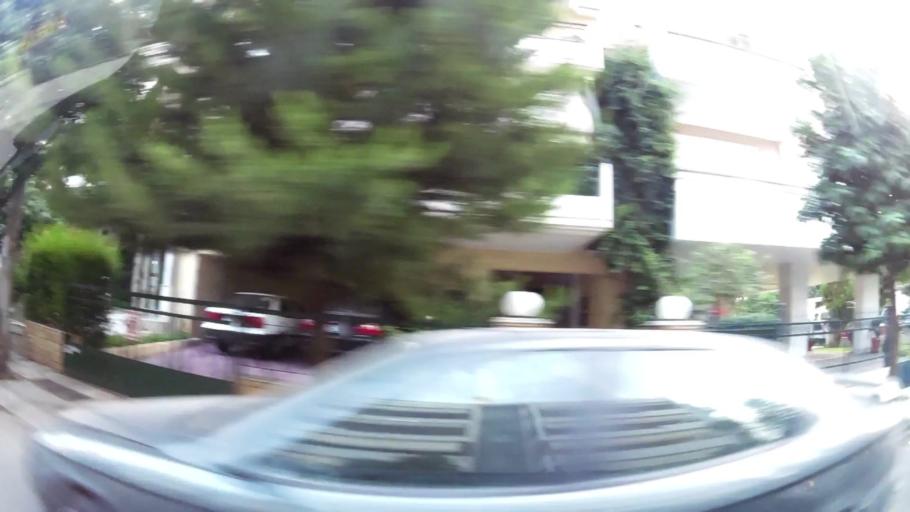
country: GR
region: Attica
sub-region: Nomarchia Athinas
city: Moskhaton
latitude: 37.9480
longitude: 23.6822
